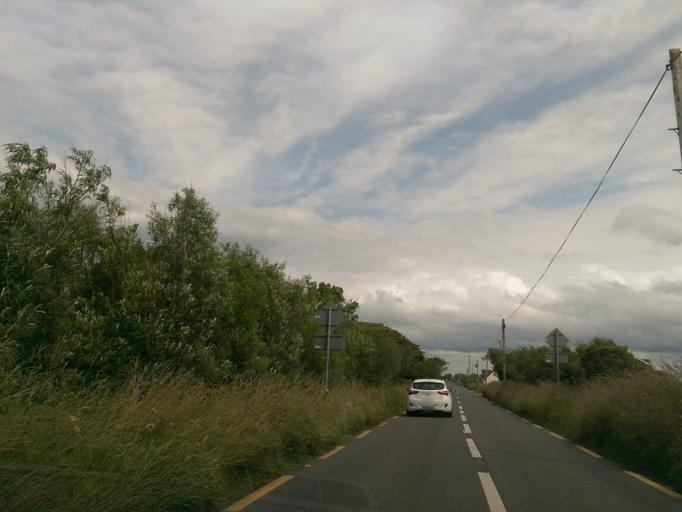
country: IE
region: Munster
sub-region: An Clar
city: Kilrush
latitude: 52.7366
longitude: -9.4919
